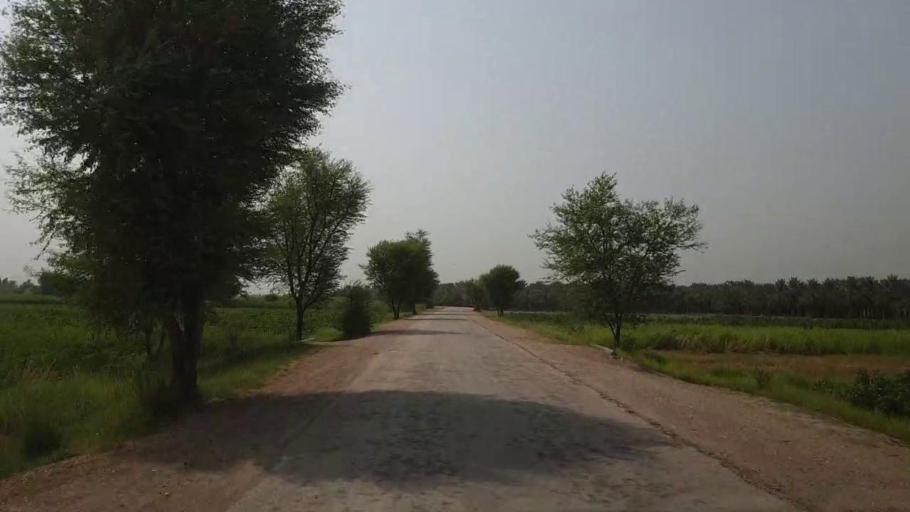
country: PK
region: Sindh
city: Gambat
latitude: 27.4315
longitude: 68.5341
